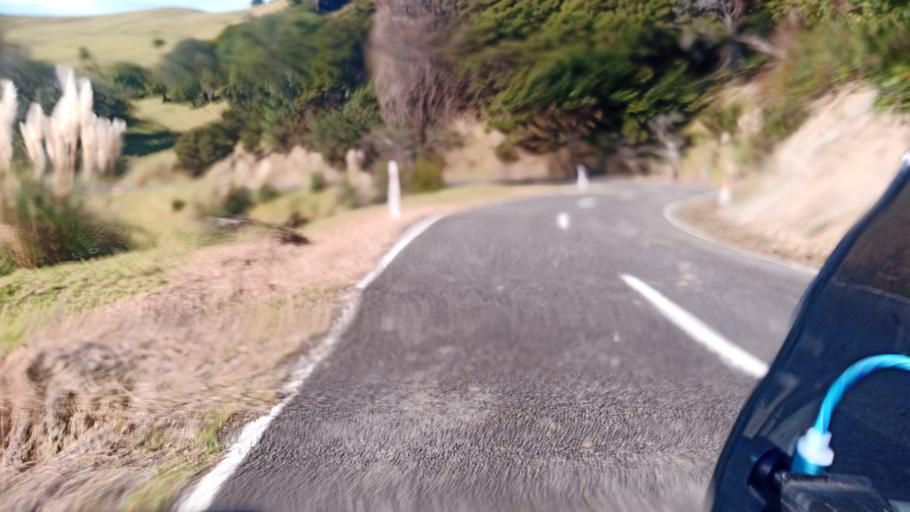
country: NZ
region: Gisborne
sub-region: Gisborne District
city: Gisborne
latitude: -38.2502
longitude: 178.3087
